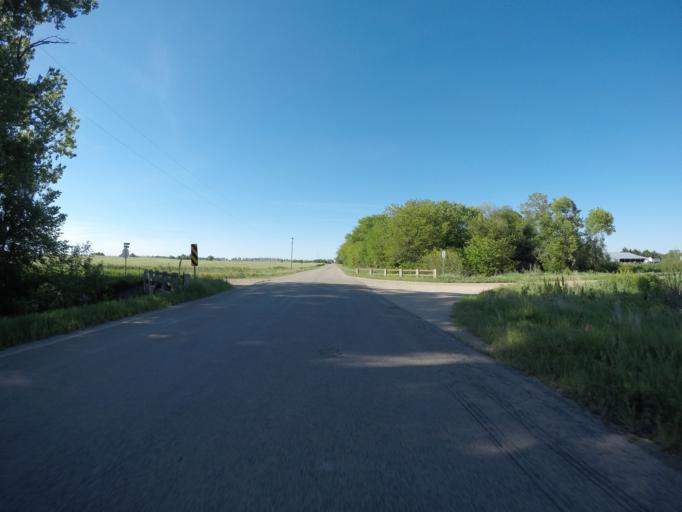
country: US
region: Kansas
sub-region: Clay County
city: Clay Center
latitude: 39.4523
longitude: -96.9980
